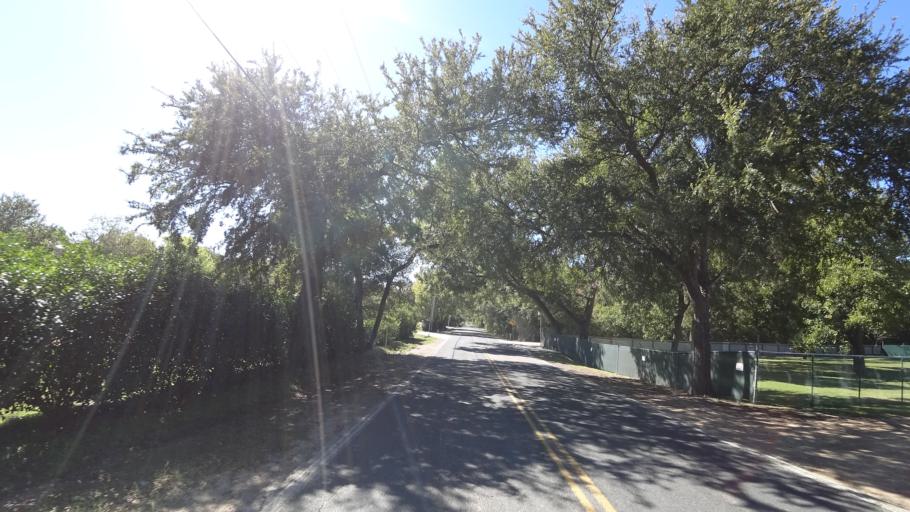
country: US
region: Texas
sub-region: Travis County
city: Hornsby Bend
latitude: 30.2931
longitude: -97.6528
